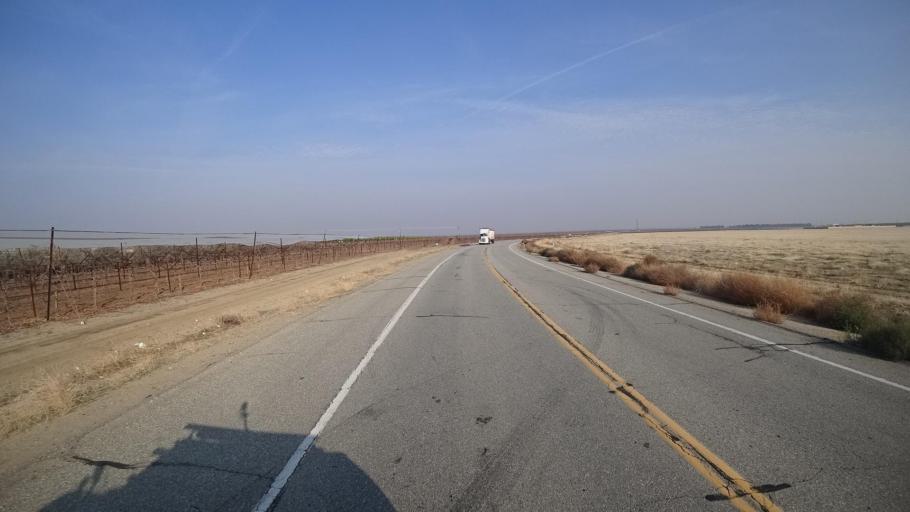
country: US
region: California
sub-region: Kern County
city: Lebec
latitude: 35.0037
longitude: -118.9436
